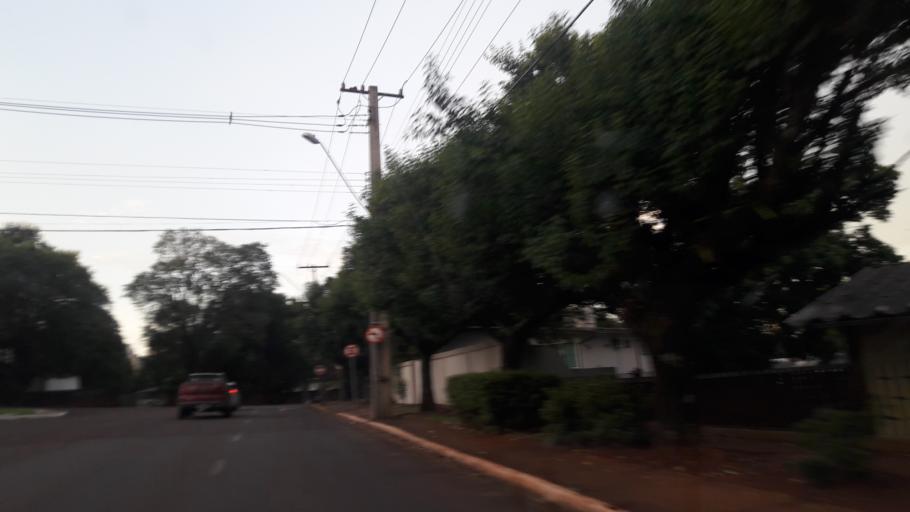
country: BR
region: Parana
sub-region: Cascavel
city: Cascavel
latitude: -24.9575
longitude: -53.4498
